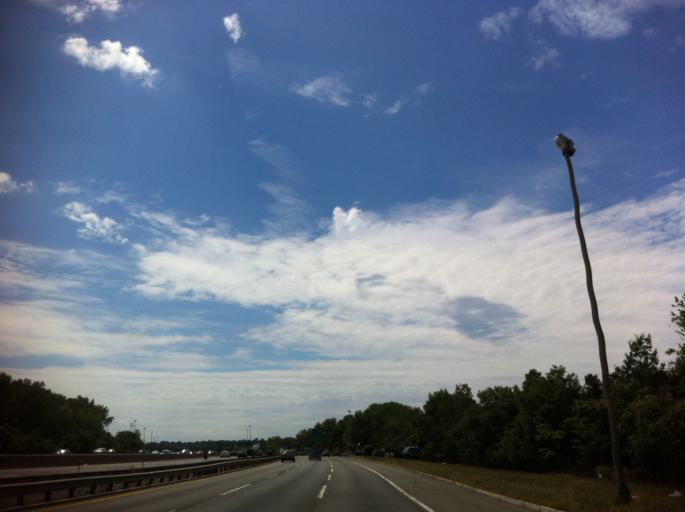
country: US
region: New Jersey
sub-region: Bergen County
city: Leonia
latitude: 40.8754
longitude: -73.9920
